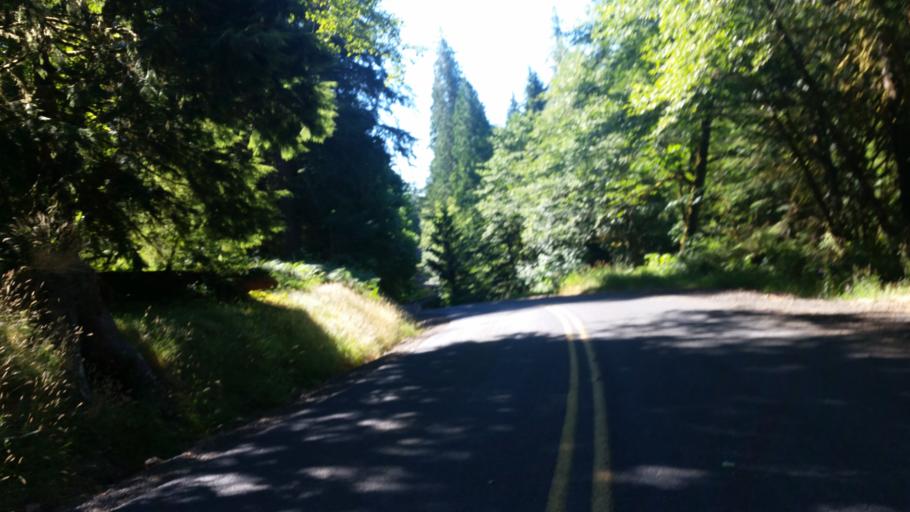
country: US
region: Washington
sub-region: Clark County
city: Amboy
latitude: 46.0099
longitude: -122.5350
